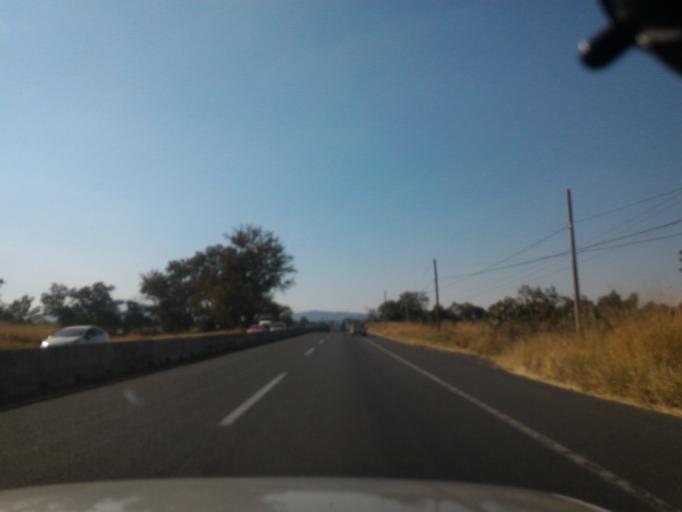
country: MX
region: Jalisco
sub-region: Ixtlahuacan de los Membrillos
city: Valle de los Girasoles [Fraccionamiento]
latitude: 20.4037
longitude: -103.1759
